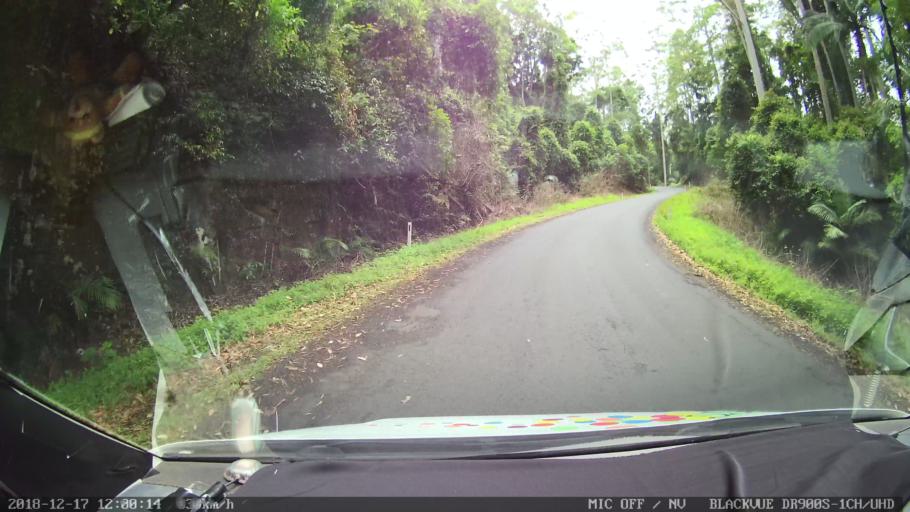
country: AU
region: New South Wales
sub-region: Kyogle
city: Kyogle
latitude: -28.5262
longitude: 152.5667
